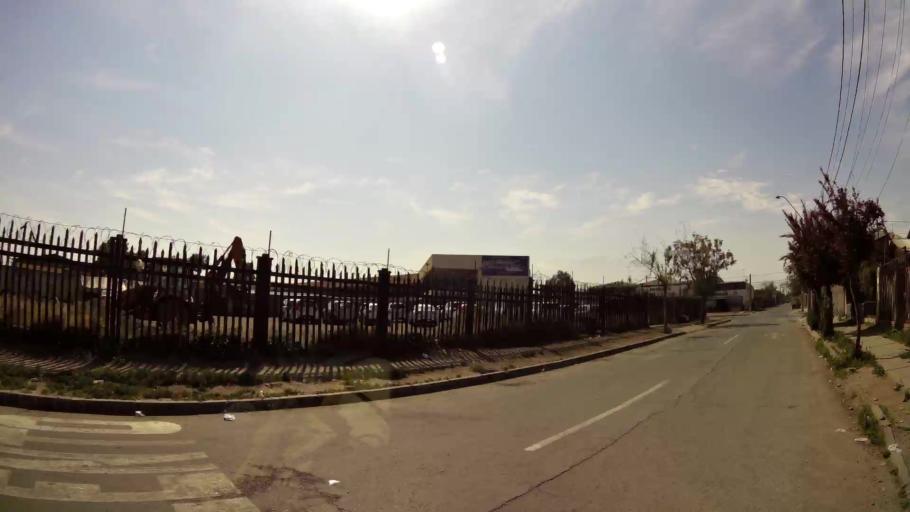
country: CL
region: Santiago Metropolitan
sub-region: Provincia de Santiago
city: La Pintana
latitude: -33.5576
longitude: -70.6483
